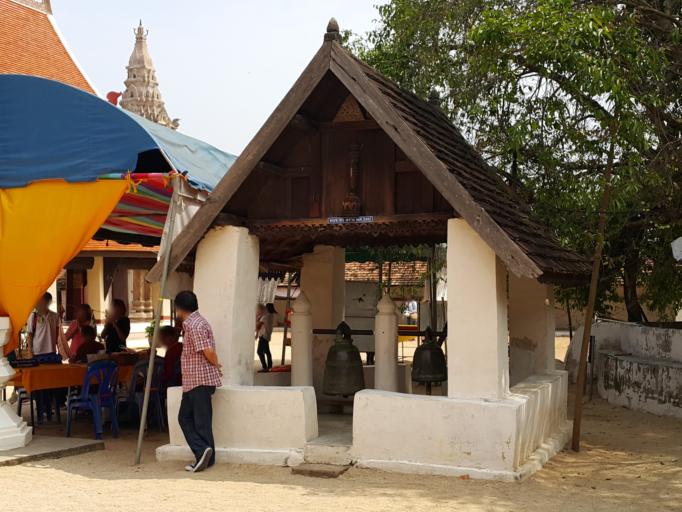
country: TH
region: Lampang
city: Ko Kha
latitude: 18.2170
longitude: 99.3889
